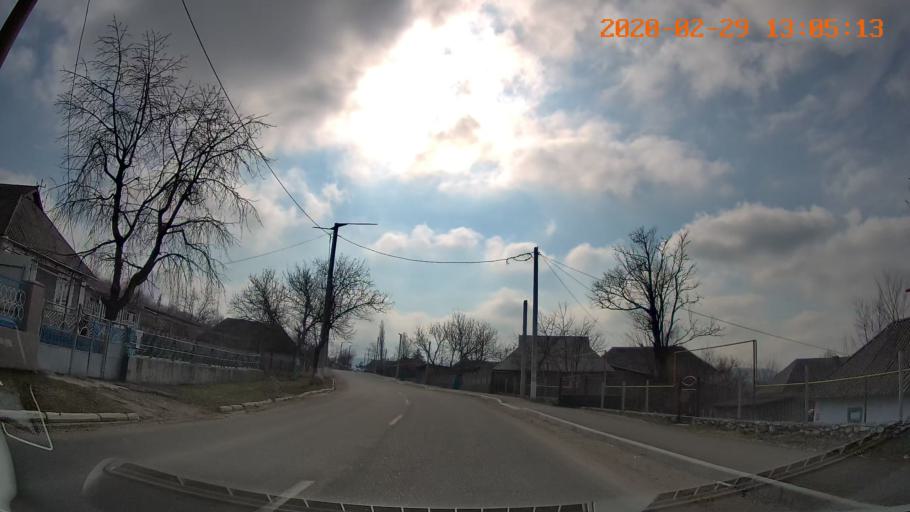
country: MD
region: Telenesti
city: Camenca
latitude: 48.0221
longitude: 28.7079
